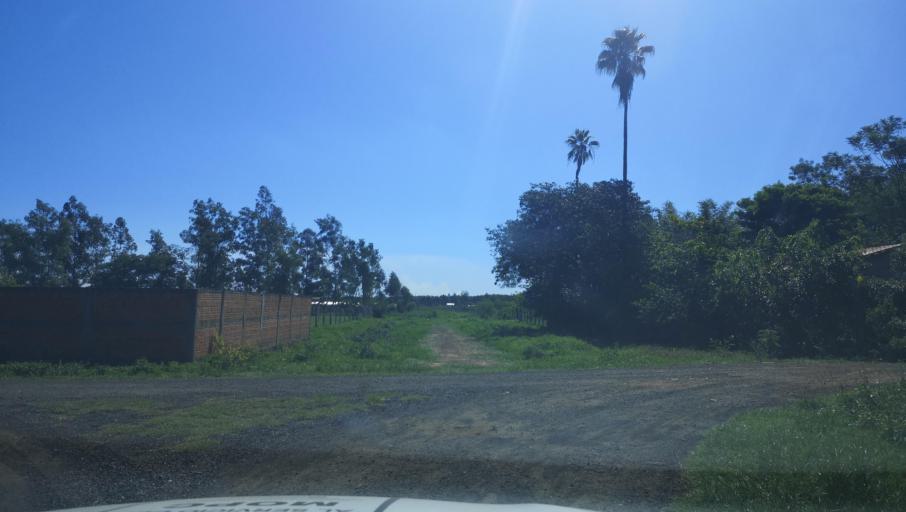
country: PY
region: Caaguazu
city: Carayao
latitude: -25.1939
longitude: -56.4053
